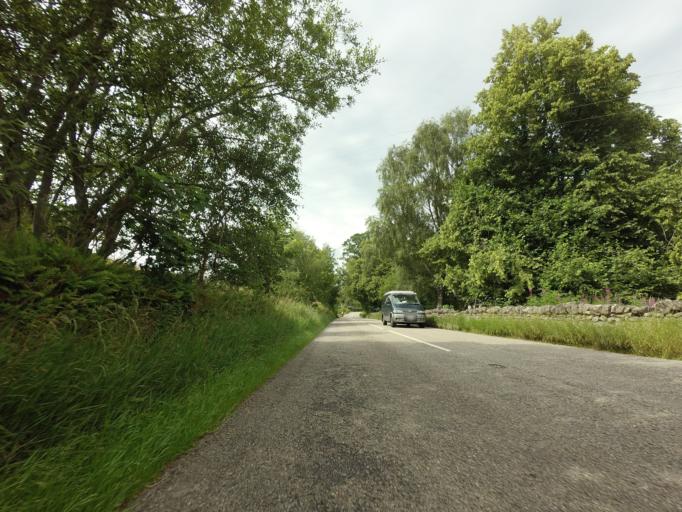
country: GB
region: Scotland
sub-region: Highland
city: Alness
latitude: 57.8557
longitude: -4.3093
